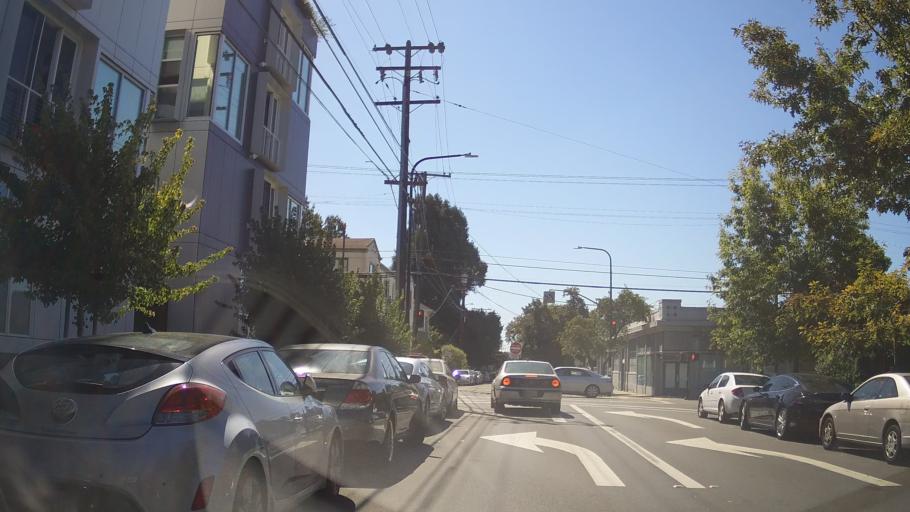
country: US
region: California
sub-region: Alameda County
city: Berkeley
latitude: 37.8648
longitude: -122.2654
